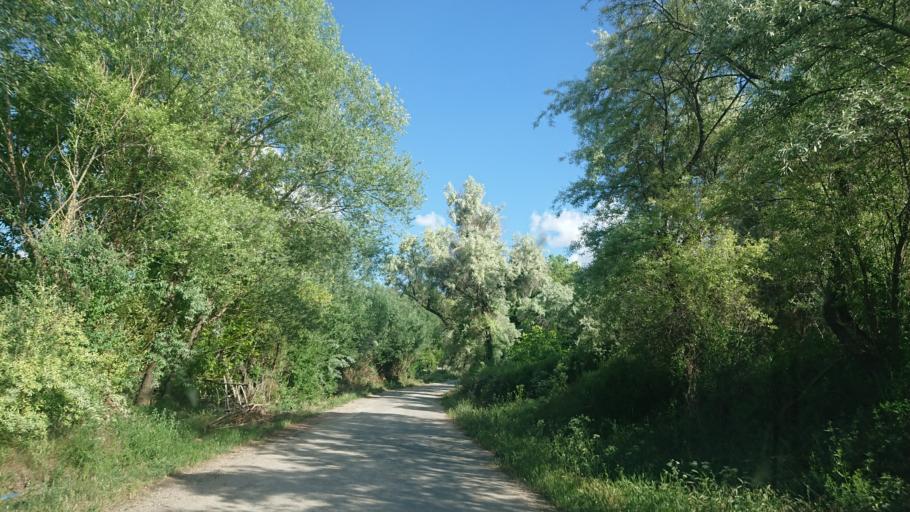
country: TR
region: Aksaray
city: Agacoren
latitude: 38.7543
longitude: 33.8874
